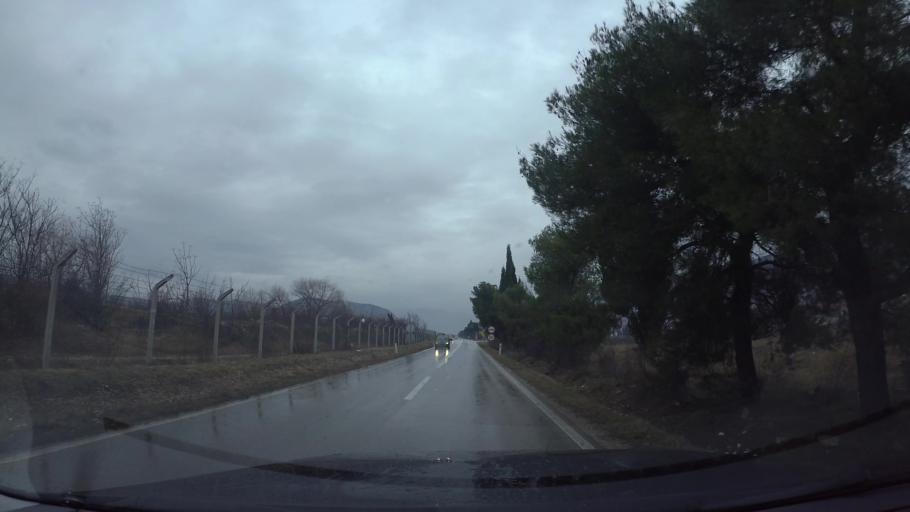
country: BA
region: Federation of Bosnia and Herzegovina
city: Rodoc
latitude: 43.2944
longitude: 17.8444
